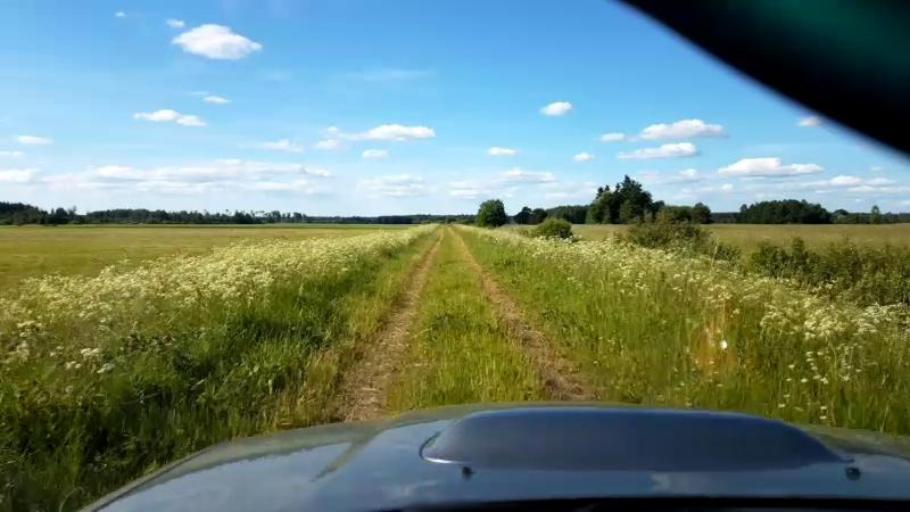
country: EE
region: Paernumaa
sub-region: Sauga vald
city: Sauga
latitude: 58.4942
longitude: 24.5917
